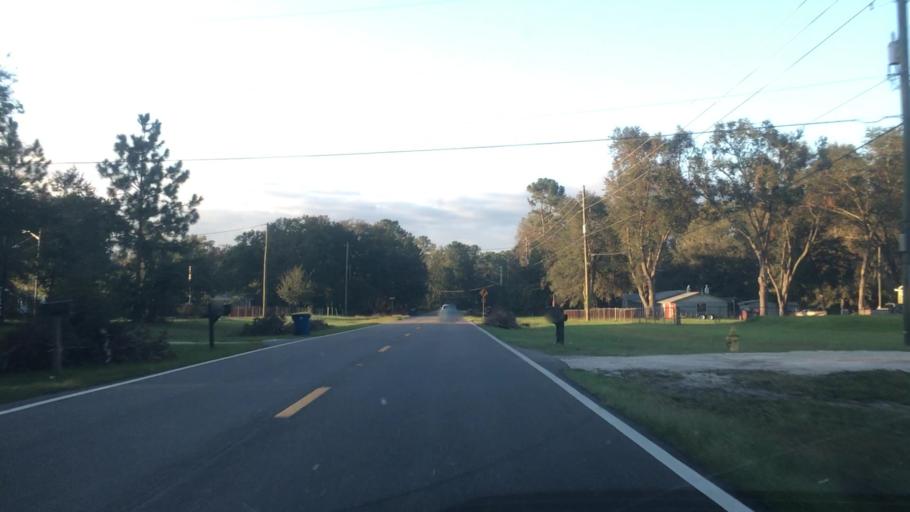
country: US
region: Florida
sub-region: Nassau County
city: Yulee
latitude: 30.4765
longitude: -81.5773
